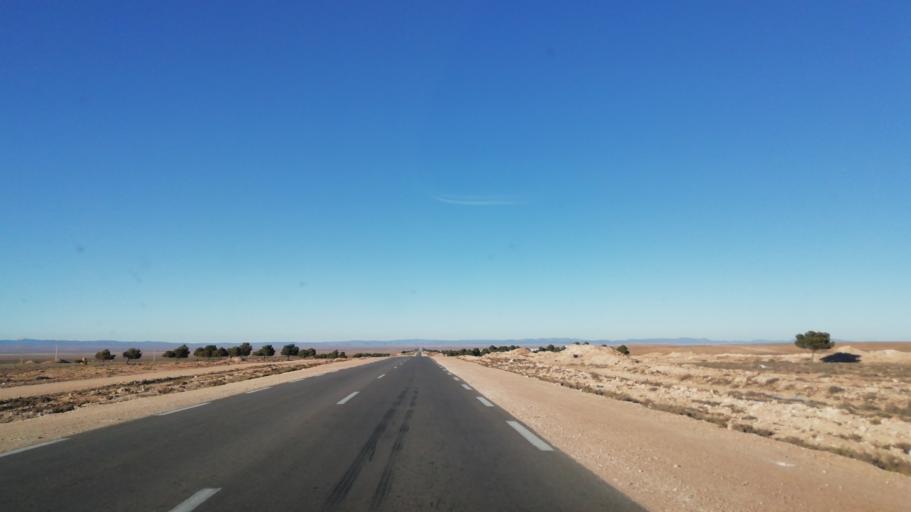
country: DZ
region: Tlemcen
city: Sebdou
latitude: 34.2888
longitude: -1.2600
